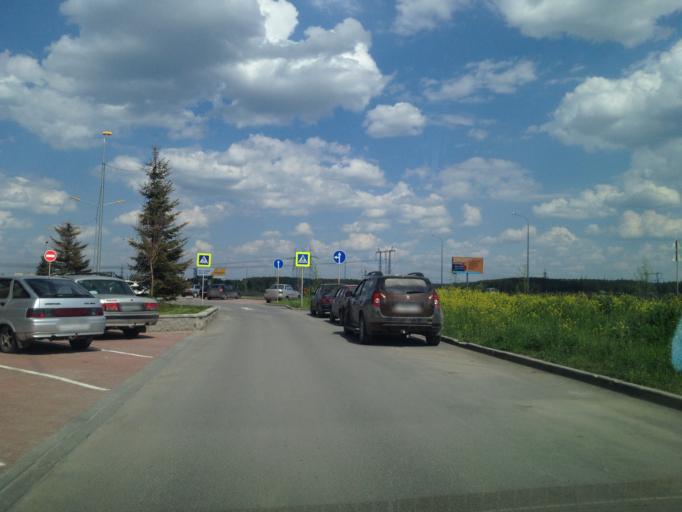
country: RU
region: Sverdlovsk
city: Sovkhoznyy
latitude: 56.7450
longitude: 60.5704
